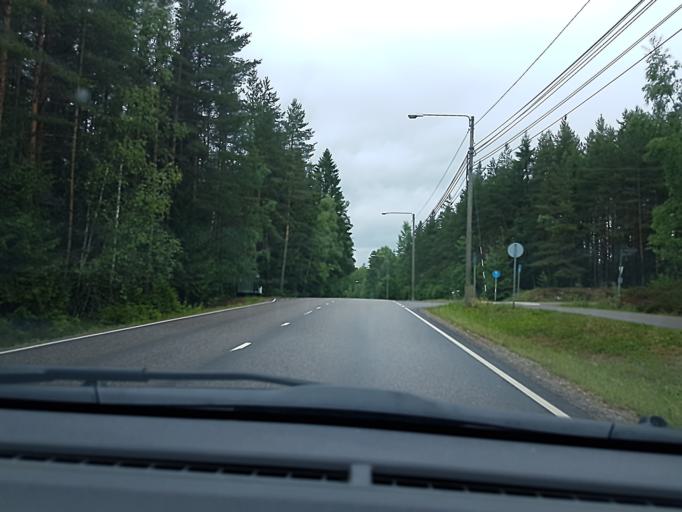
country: FI
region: Uusimaa
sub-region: Helsinki
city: Pornainen
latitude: 60.4708
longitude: 25.3823
